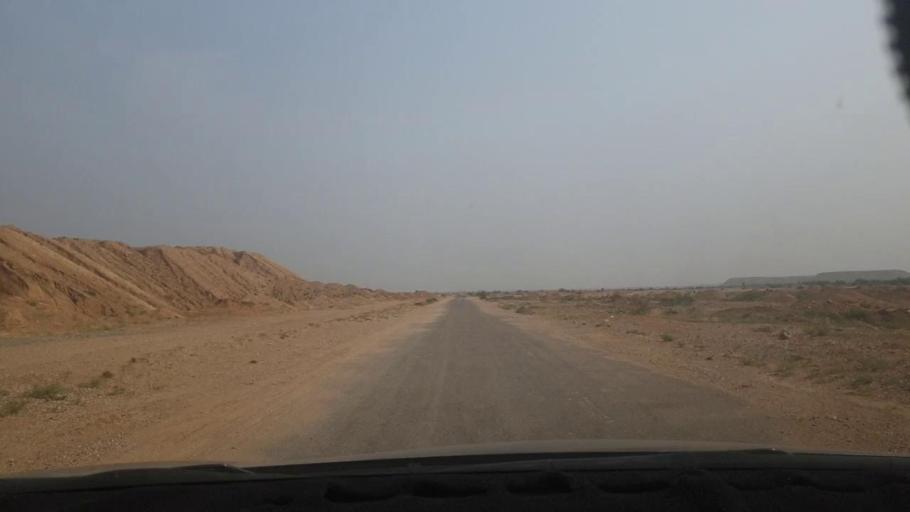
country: PK
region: Sindh
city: Matiari
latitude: 25.5801
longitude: 68.3140
